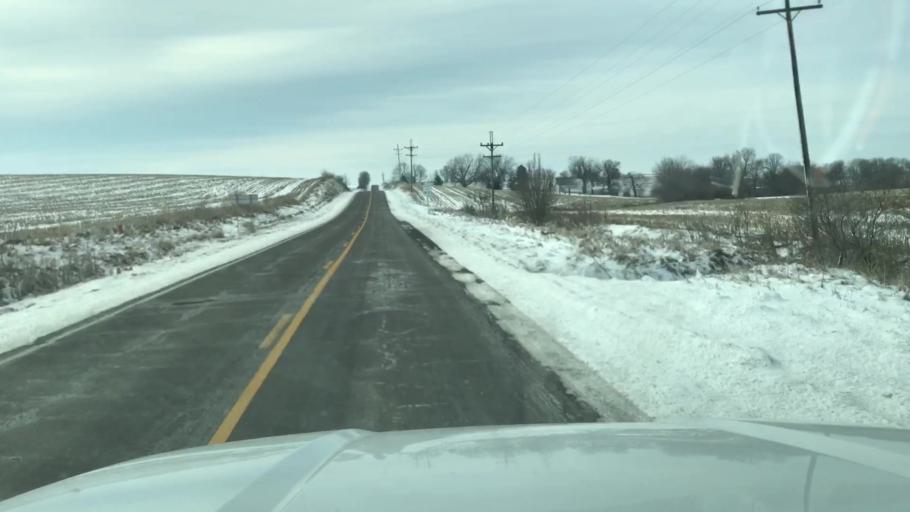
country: US
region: Missouri
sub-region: Holt County
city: Oregon
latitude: 40.0787
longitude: -95.1355
